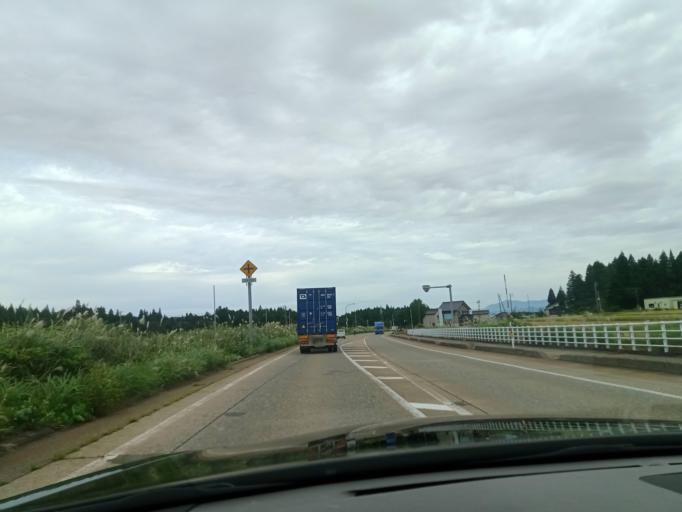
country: JP
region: Niigata
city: Arai
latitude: 36.9948
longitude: 138.2181
